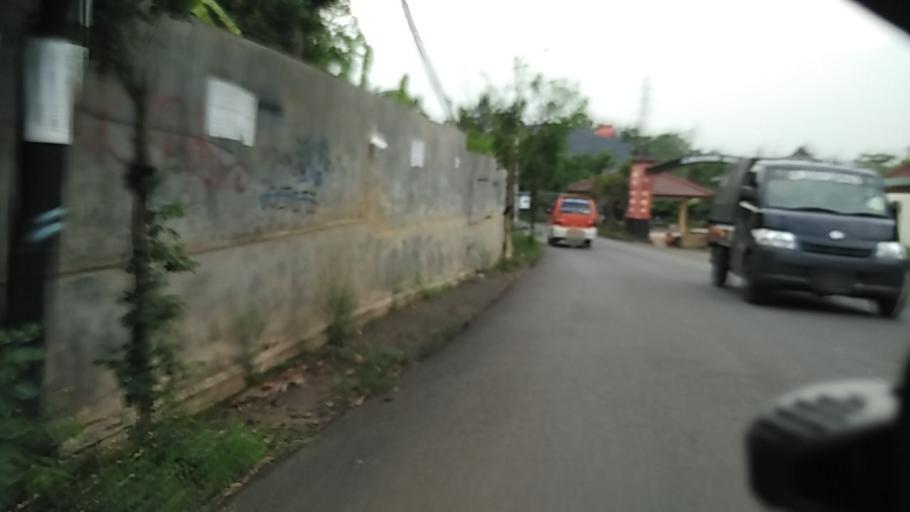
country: ID
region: Central Java
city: Semarang
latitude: -7.0659
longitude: 110.4380
